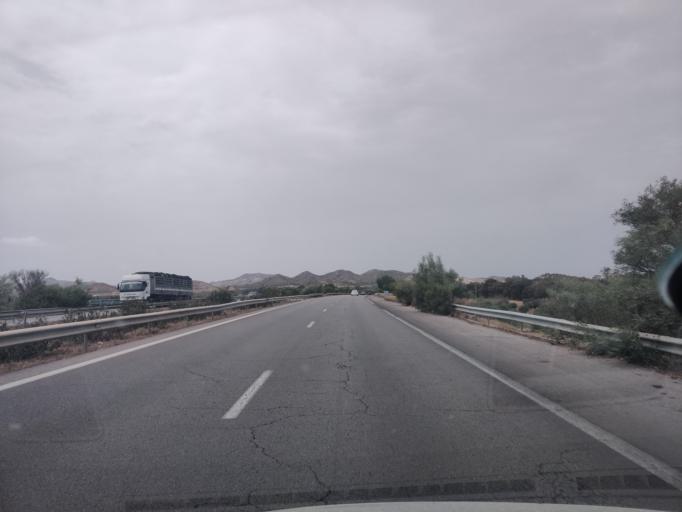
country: TN
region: Susah
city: Harqalah
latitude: 36.2133
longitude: 10.4233
